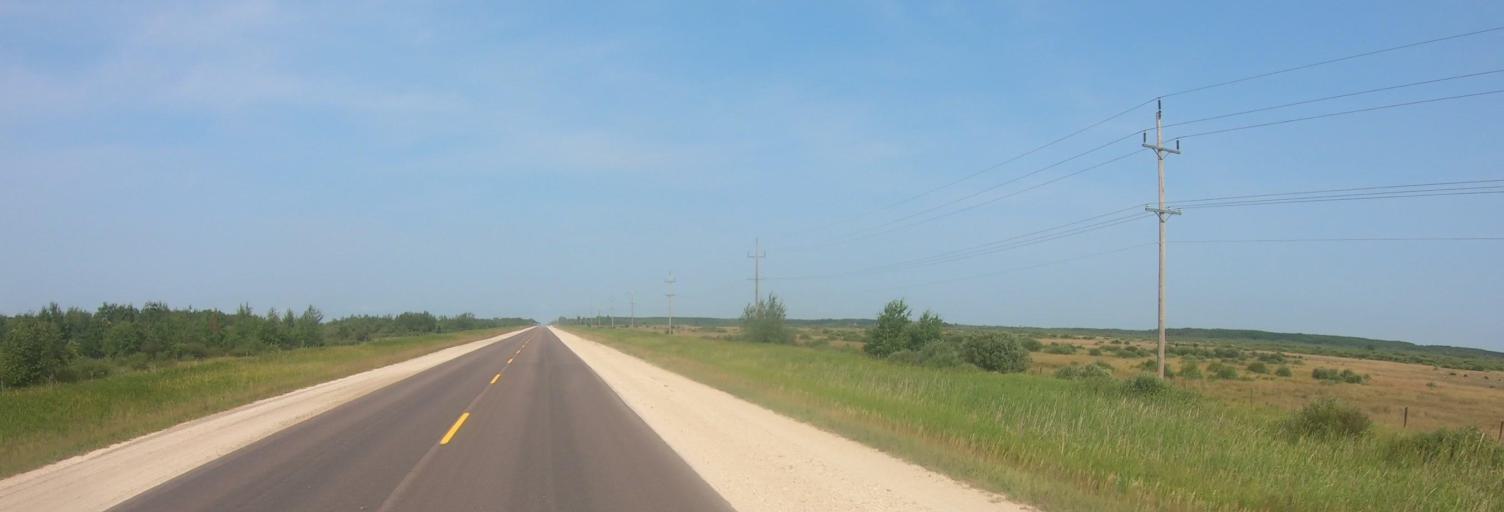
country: CA
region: Manitoba
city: La Broquerie
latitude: 49.2755
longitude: -96.4924
